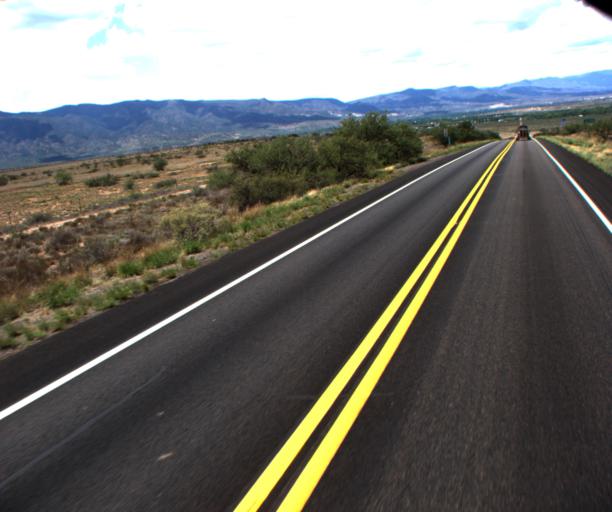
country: US
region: Arizona
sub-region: Yavapai County
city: Camp Verde
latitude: 34.5075
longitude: -111.7661
